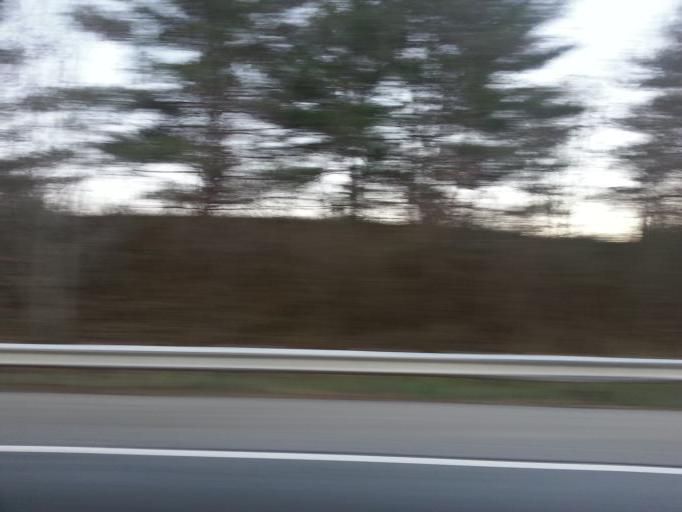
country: US
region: North Carolina
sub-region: Haywood County
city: Cove Creek
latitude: 35.5751
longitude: -82.9766
